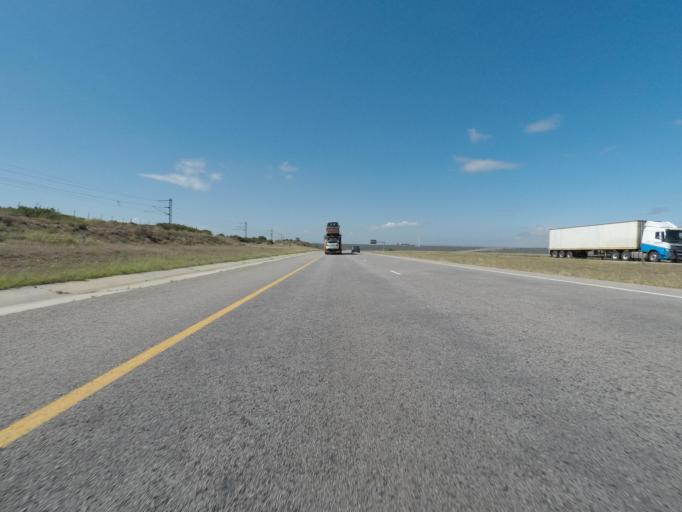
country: ZA
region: Eastern Cape
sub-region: Nelson Mandela Bay Metropolitan Municipality
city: Port Elizabeth
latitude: -33.7829
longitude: 25.6651
